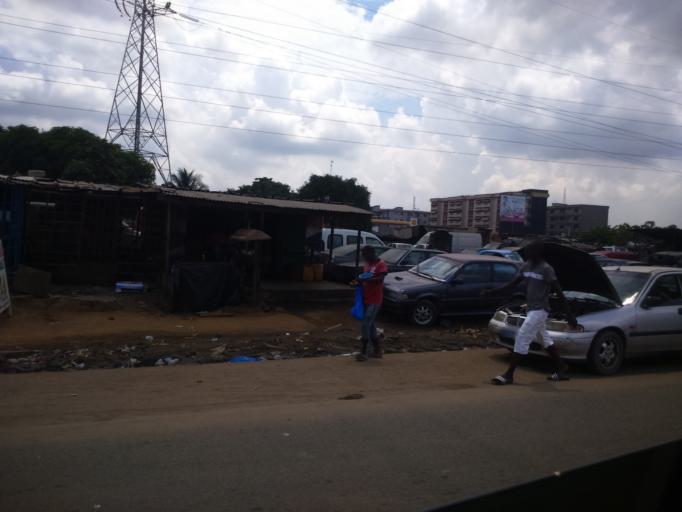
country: CI
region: Lagunes
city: Abidjan
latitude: 5.3553
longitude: -4.0859
